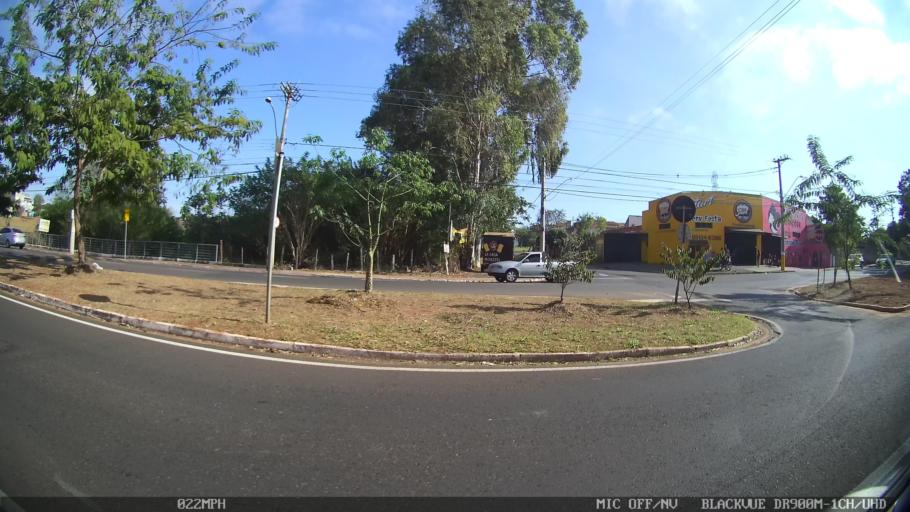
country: BR
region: Sao Paulo
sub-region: Sao Jose Do Rio Preto
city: Sao Jose do Rio Preto
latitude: -20.7954
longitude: -49.4260
